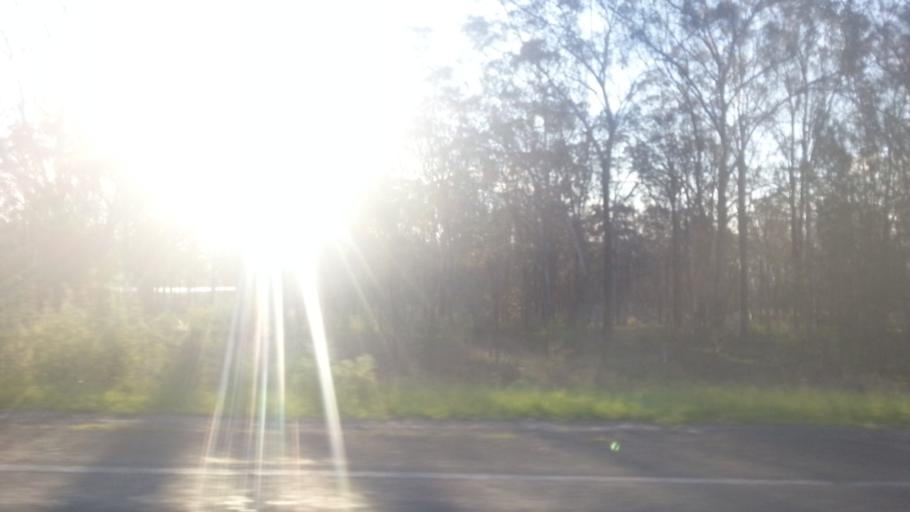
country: AU
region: New South Wales
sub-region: Camden
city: Camden South
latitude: -34.1065
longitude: 150.6986
